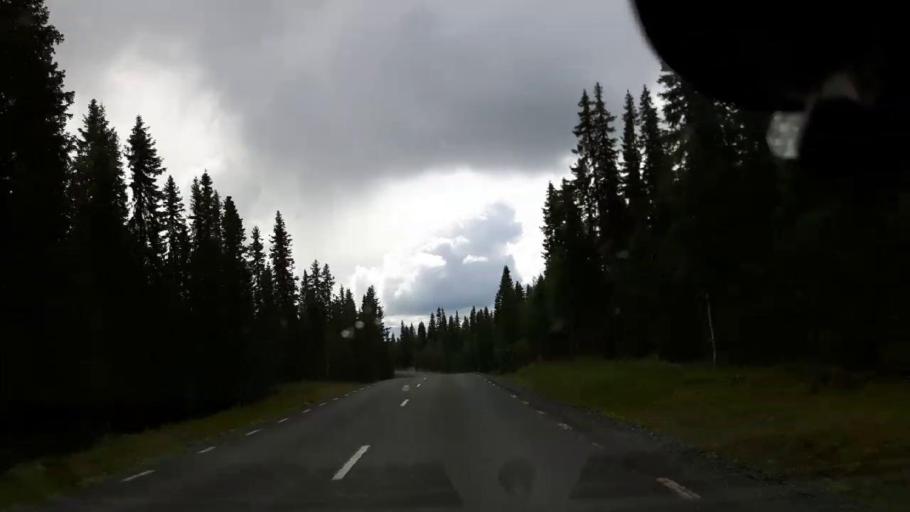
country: SE
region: Jaemtland
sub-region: Krokoms Kommun
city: Valla
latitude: 63.4429
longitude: 13.8262
